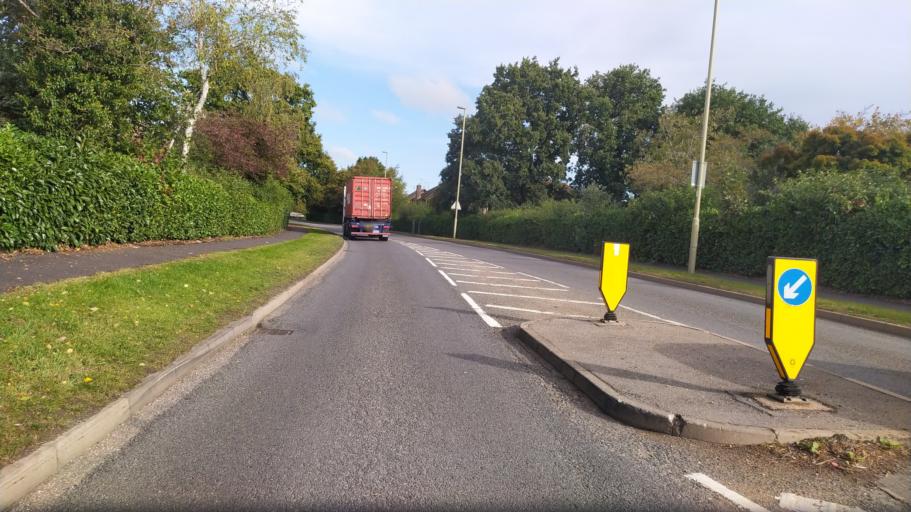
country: GB
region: England
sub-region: Hampshire
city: Hook
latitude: 51.2850
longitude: -0.9535
